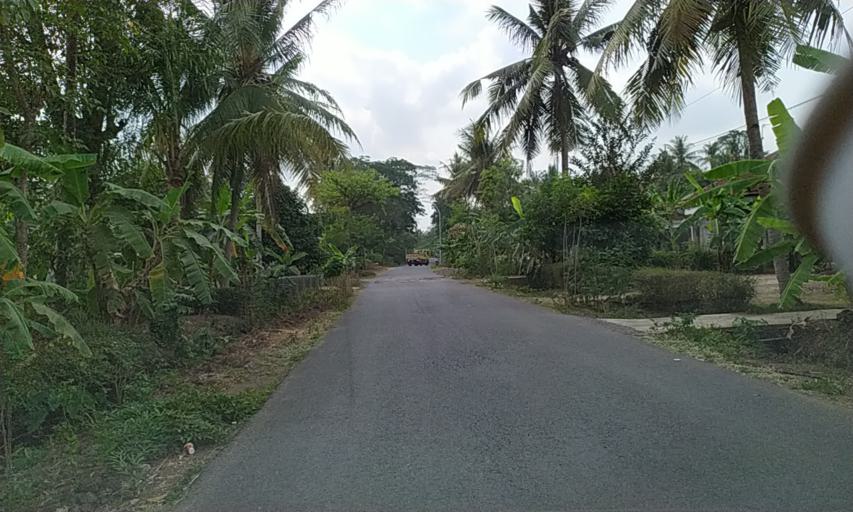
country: ID
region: Central Java
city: Kedungwringin
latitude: -7.4849
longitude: 108.7667
